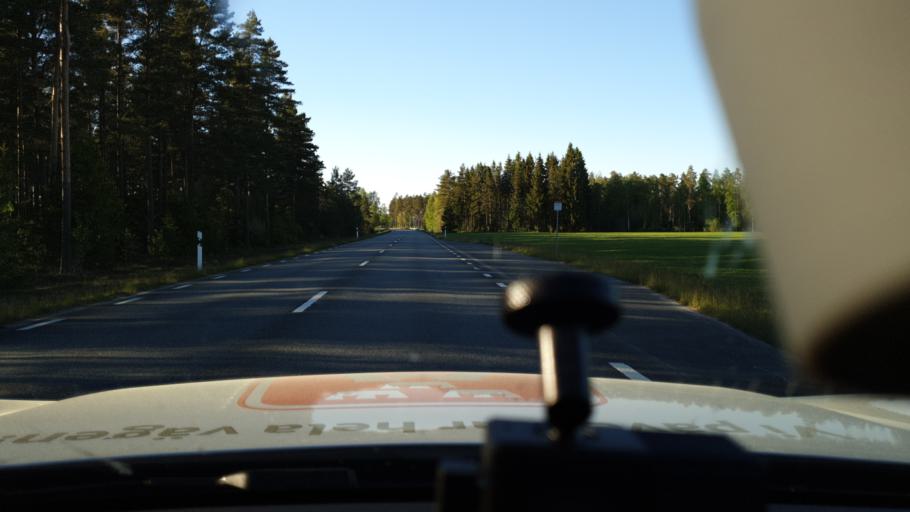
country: SE
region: Joenkoeping
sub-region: Eksjo Kommun
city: Eksjoe
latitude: 57.6129
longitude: 14.9701
